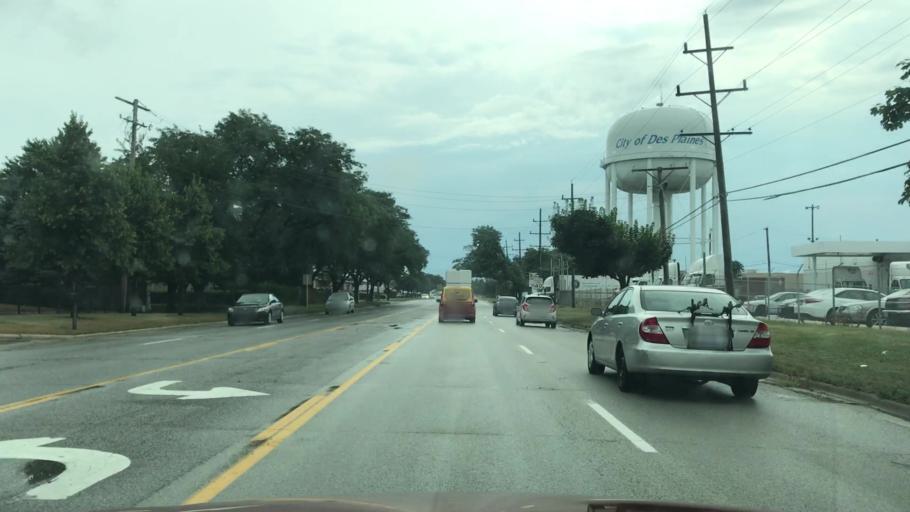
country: US
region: Illinois
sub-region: Cook County
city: Mount Prospect
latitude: 42.0228
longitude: -87.9276
